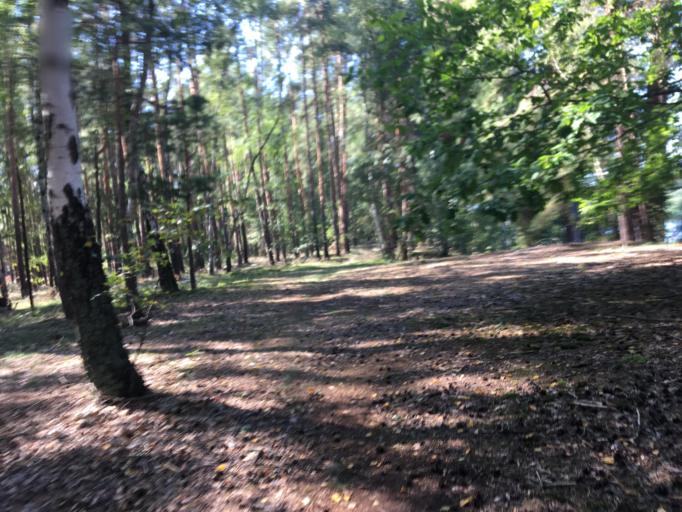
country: DE
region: Brandenburg
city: Gross Koris
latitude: 52.2033
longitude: 13.7429
